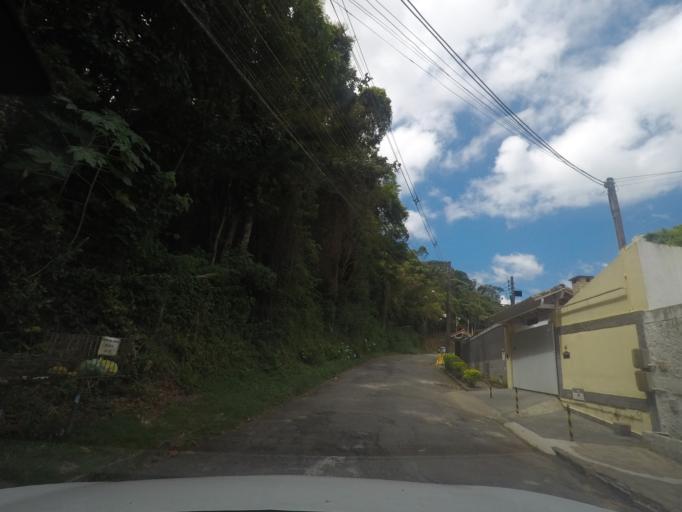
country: BR
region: Rio de Janeiro
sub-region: Teresopolis
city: Teresopolis
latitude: -22.4022
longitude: -42.9794
